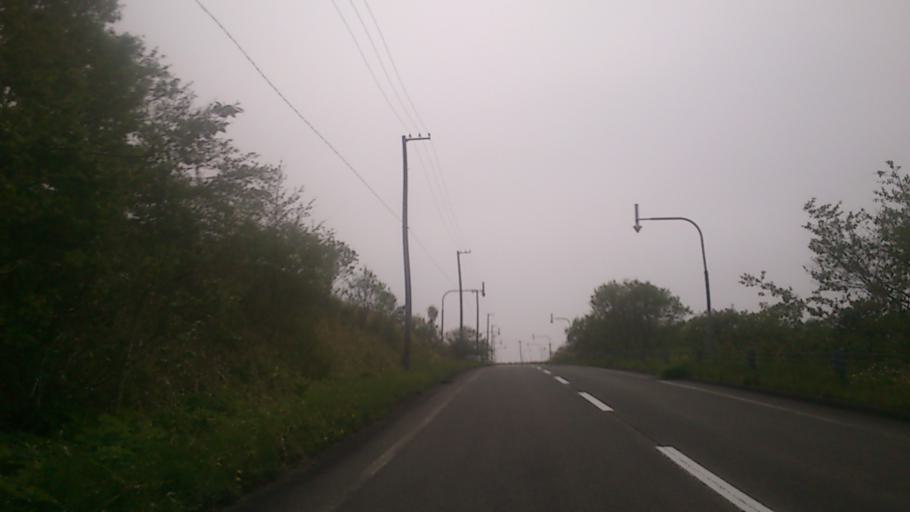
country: JP
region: Hokkaido
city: Nemuro
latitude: 43.1760
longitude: 145.3204
